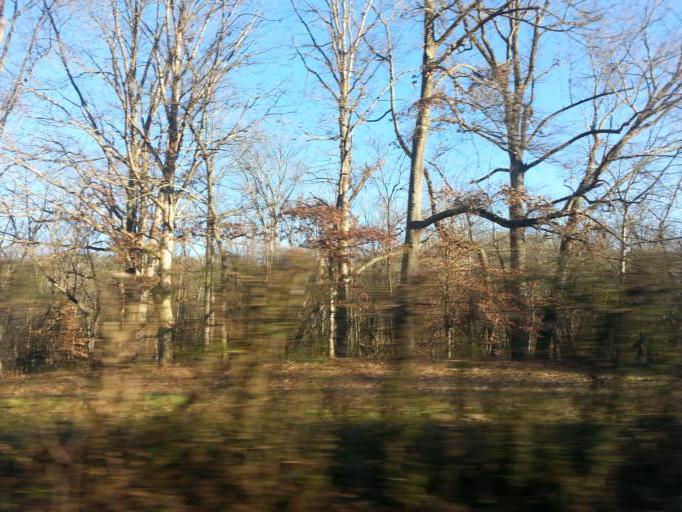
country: US
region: Tennessee
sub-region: Anderson County
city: Rocky Top
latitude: 36.1735
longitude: -84.1656
